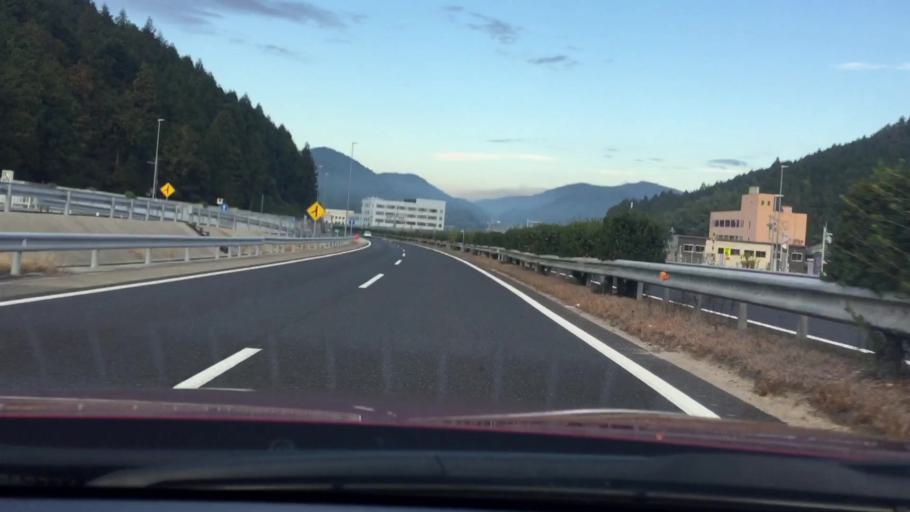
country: JP
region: Hyogo
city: Himeji
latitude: 34.9631
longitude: 134.6930
